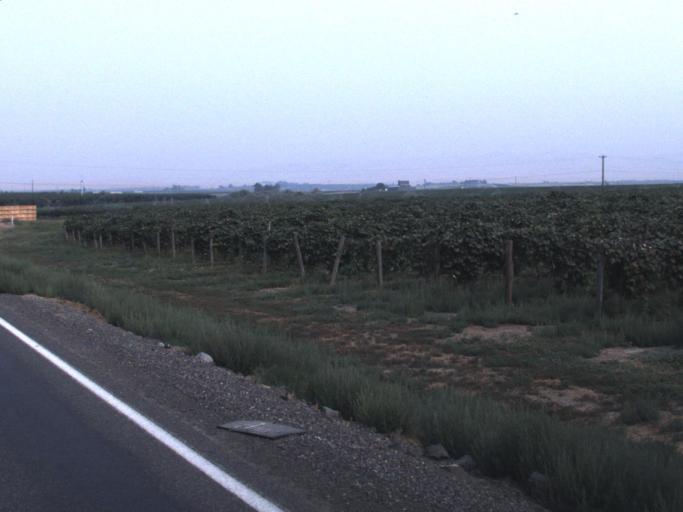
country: US
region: Washington
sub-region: Yakima County
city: Sunnyside
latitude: 46.3521
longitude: -119.9791
